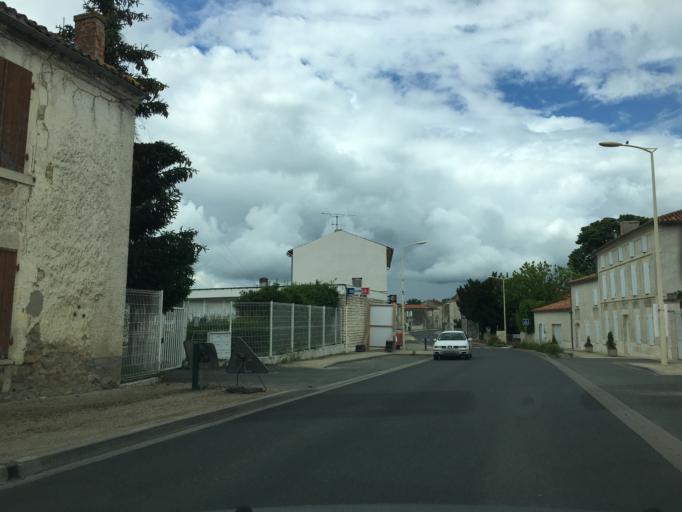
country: FR
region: Poitou-Charentes
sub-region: Departement de la Charente-Maritime
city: Saint-Jean-d'Angely
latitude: 46.0449
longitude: -0.5128
